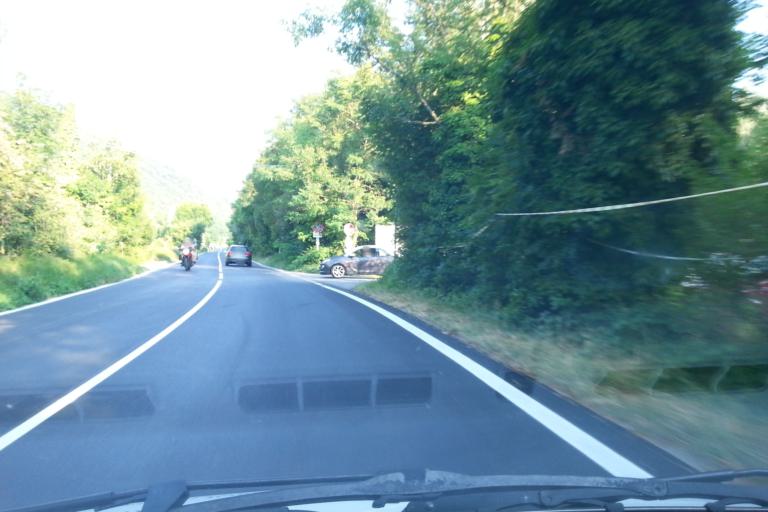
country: IT
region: Piedmont
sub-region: Provincia di Torino
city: Trana
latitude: 45.0523
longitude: 7.3971
